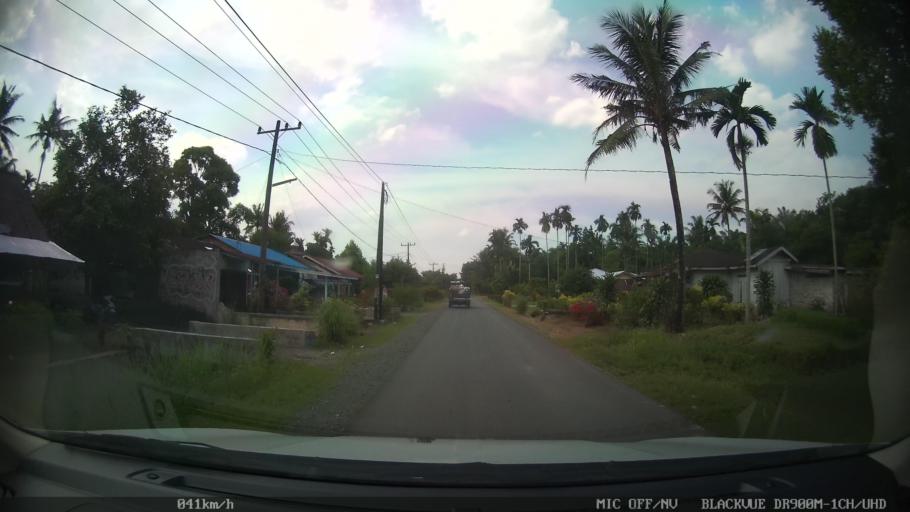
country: ID
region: North Sumatra
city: Binjai
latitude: 3.6398
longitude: 98.5175
